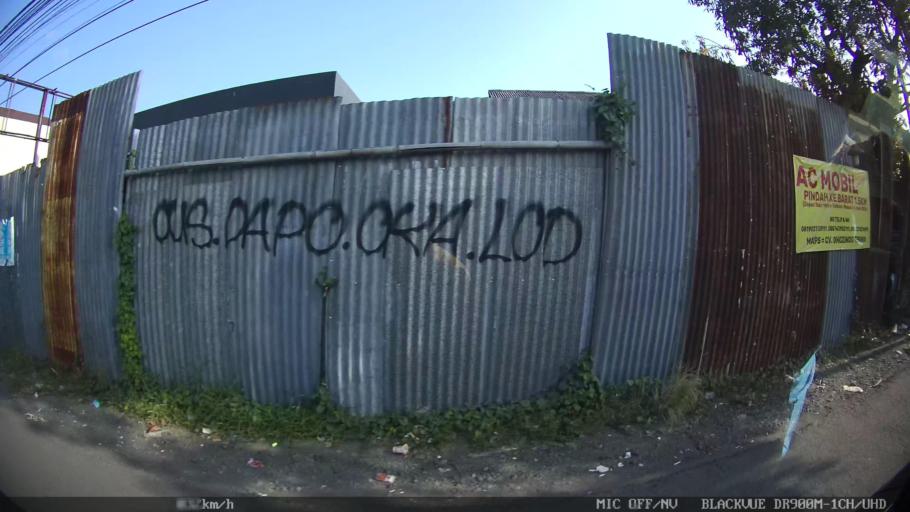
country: ID
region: Daerah Istimewa Yogyakarta
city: Gamping Lor
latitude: -7.7787
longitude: 110.3385
